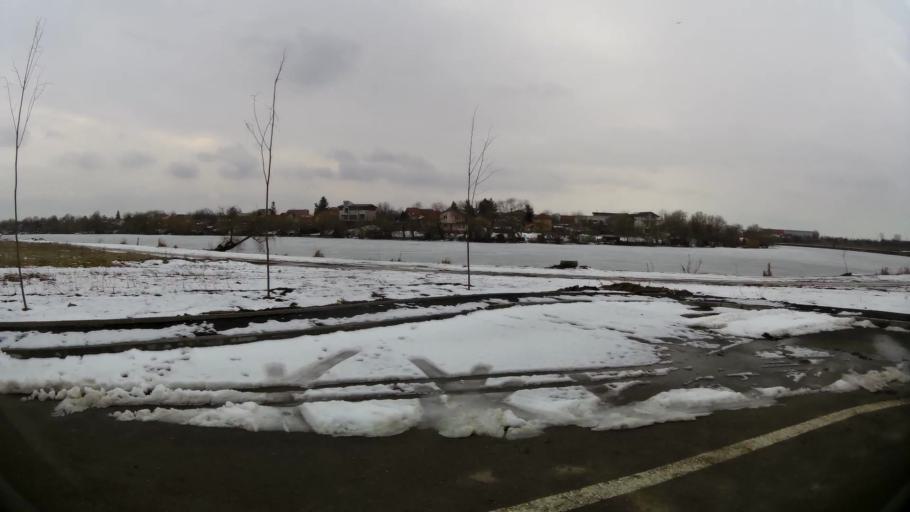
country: RO
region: Ilfov
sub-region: Comuna Tunari
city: Tunari
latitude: 44.5523
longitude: 26.1512
